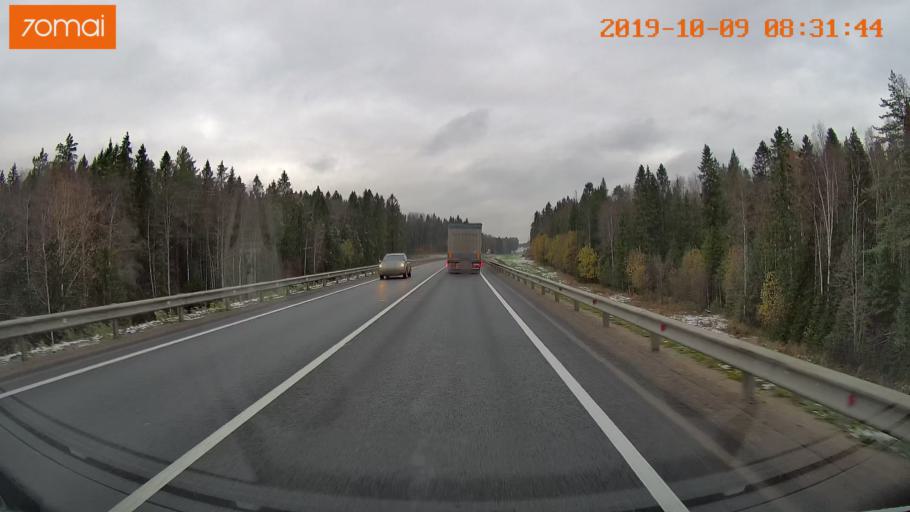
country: RU
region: Vologda
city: Gryazovets
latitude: 58.8577
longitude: 40.2001
